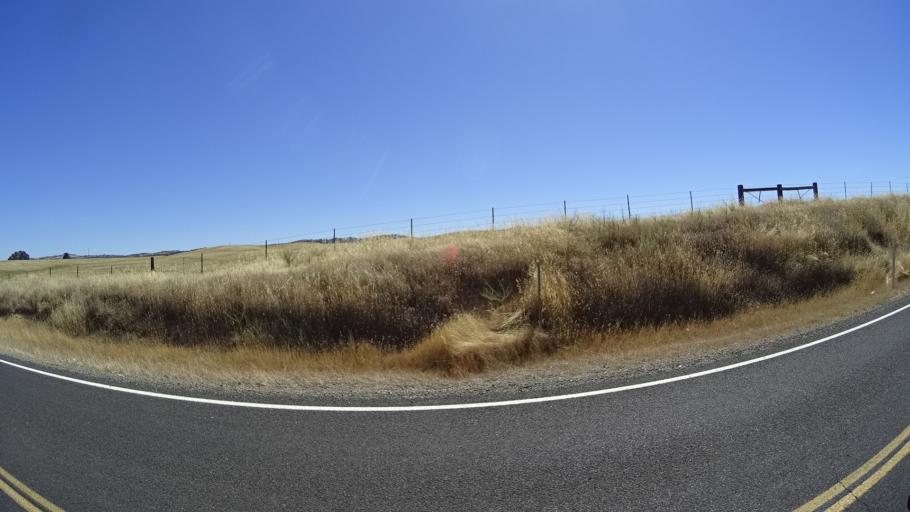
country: US
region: California
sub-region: Calaveras County
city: Rancho Calaveras
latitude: 38.0486
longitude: -120.8601
